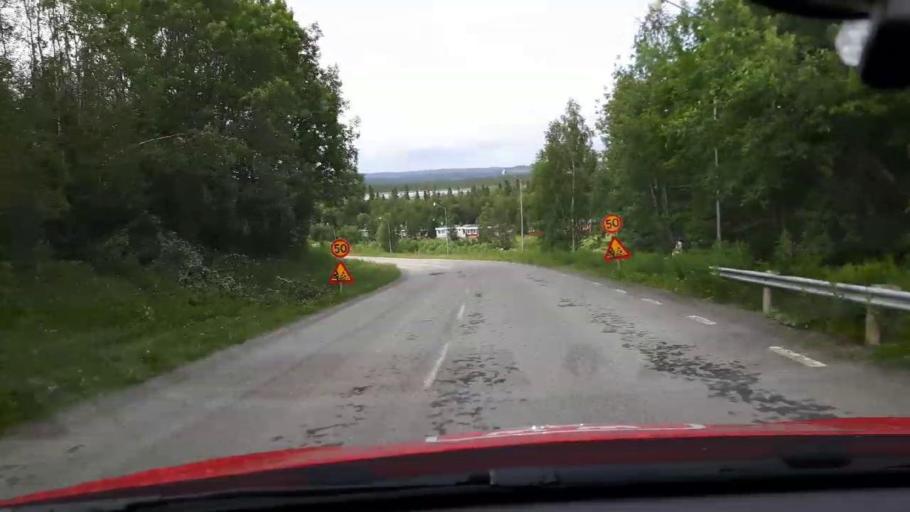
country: SE
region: Jaemtland
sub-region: Are Kommun
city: Are
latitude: 63.2539
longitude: 12.4536
